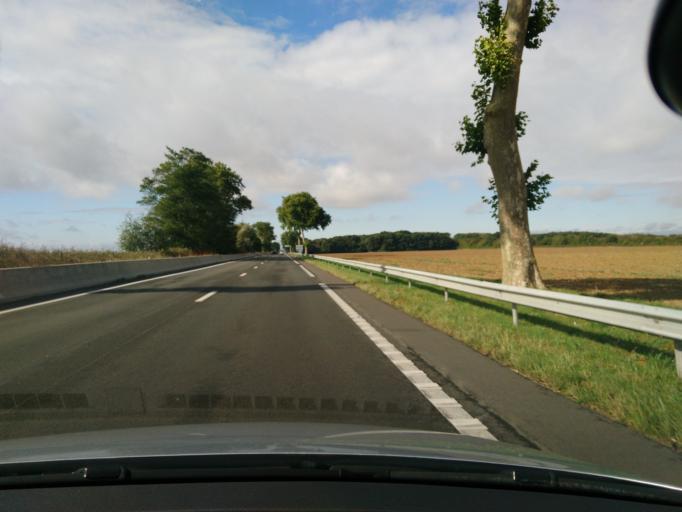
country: FR
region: Centre
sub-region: Departement d'Eure-et-Loir
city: Cherisy
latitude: 48.7547
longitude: 1.4687
